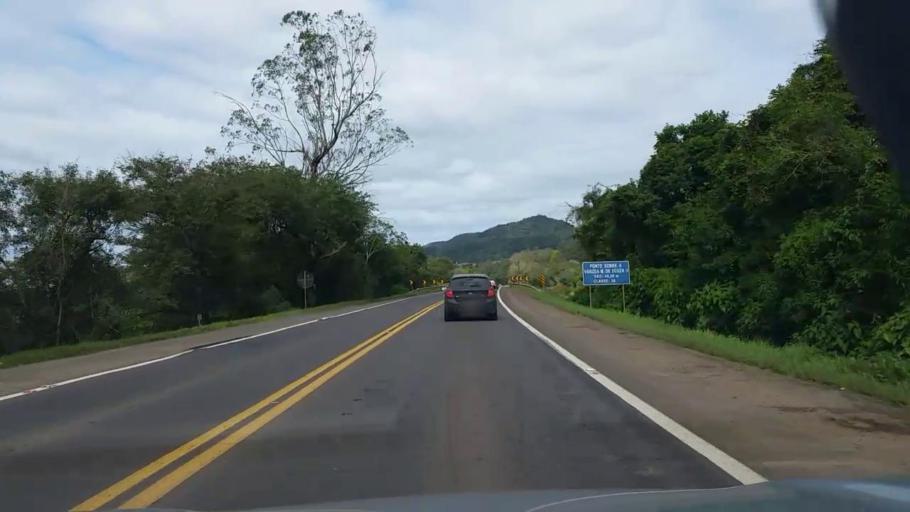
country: BR
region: Rio Grande do Sul
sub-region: Arroio Do Meio
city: Arroio do Meio
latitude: -29.3473
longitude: -52.0717
